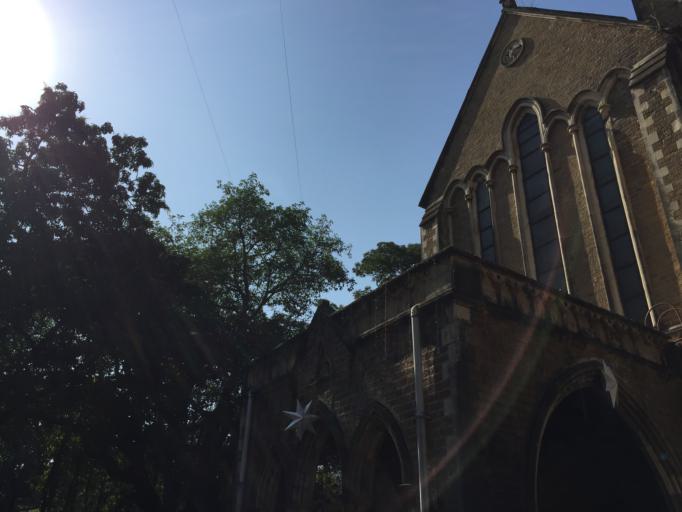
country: IN
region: Maharashtra
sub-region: Raigarh
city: Uran
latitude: 18.9067
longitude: 72.8165
